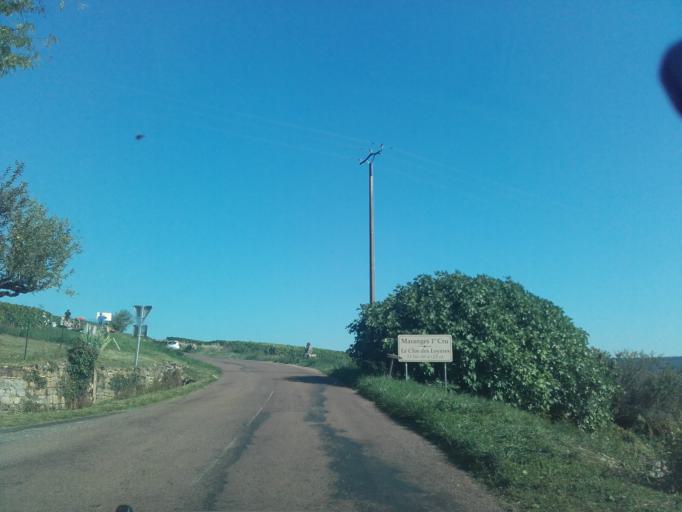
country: FR
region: Bourgogne
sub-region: Departement de la Cote-d'Or
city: Nolay
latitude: 46.9093
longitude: 4.6554
